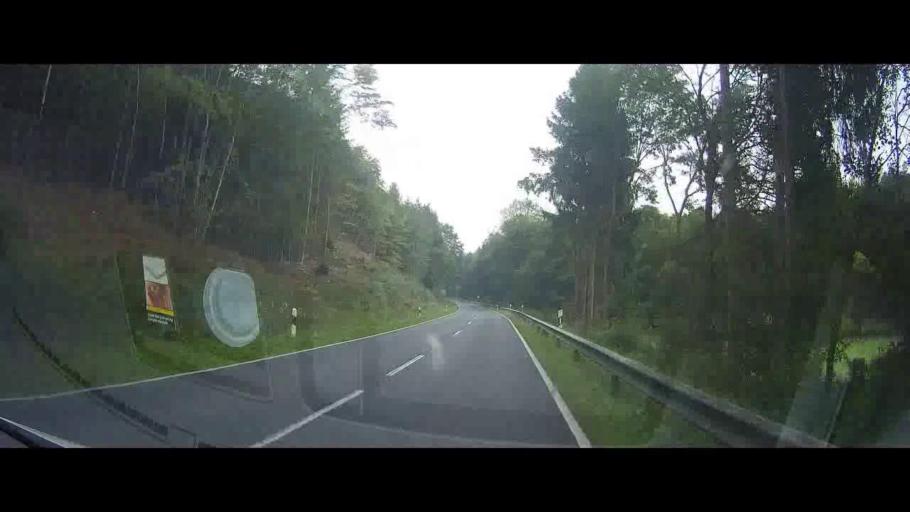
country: DE
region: Lower Saxony
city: Adelebsen
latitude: 51.5745
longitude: 9.7055
